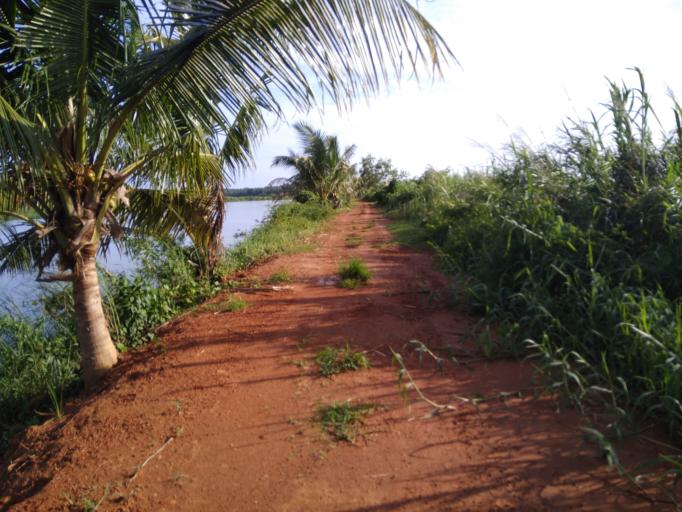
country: IN
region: Kerala
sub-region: Thrissur District
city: Trichur
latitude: 10.5166
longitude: 76.1593
